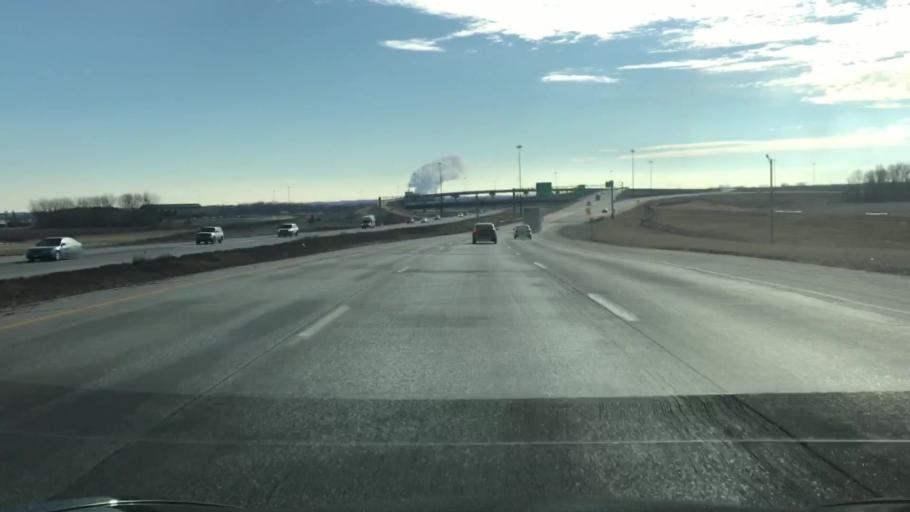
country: US
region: Nebraska
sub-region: Douglas County
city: Omaha
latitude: 41.2405
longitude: -95.9035
